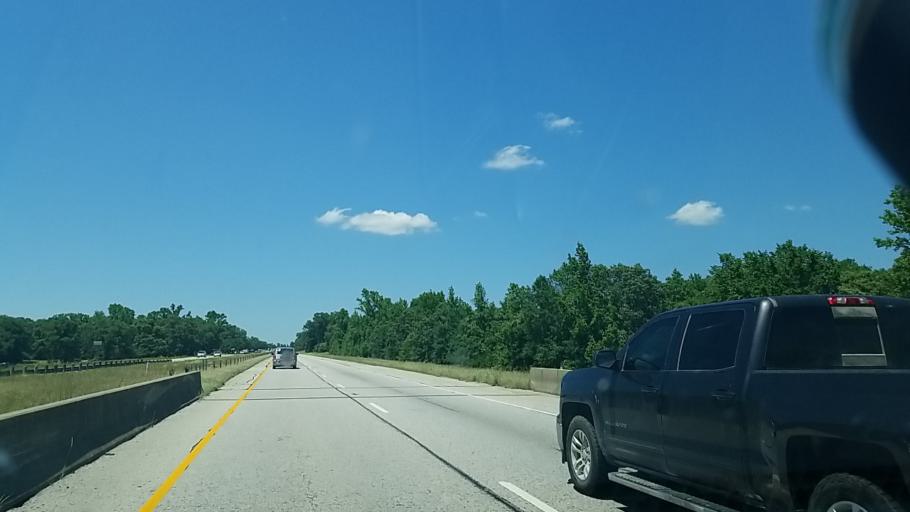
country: US
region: Texas
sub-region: Leon County
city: Centerville
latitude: 31.1892
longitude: -95.9920
